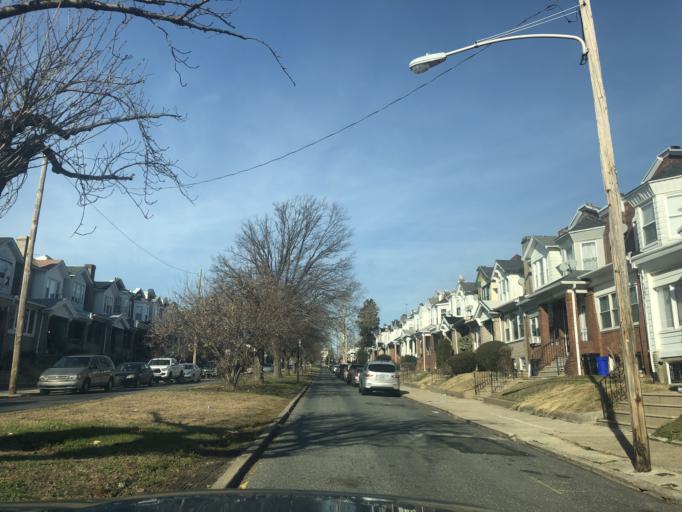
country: US
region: Pennsylvania
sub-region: Delaware County
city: Millbourne
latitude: 39.9724
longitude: -75.2478
